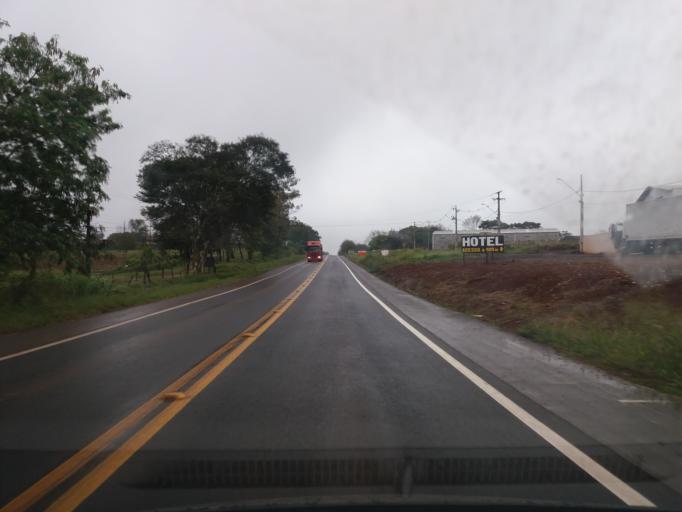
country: BR
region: Parana
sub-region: Realeza
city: Realeza
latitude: -25.5030
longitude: -53.5959
